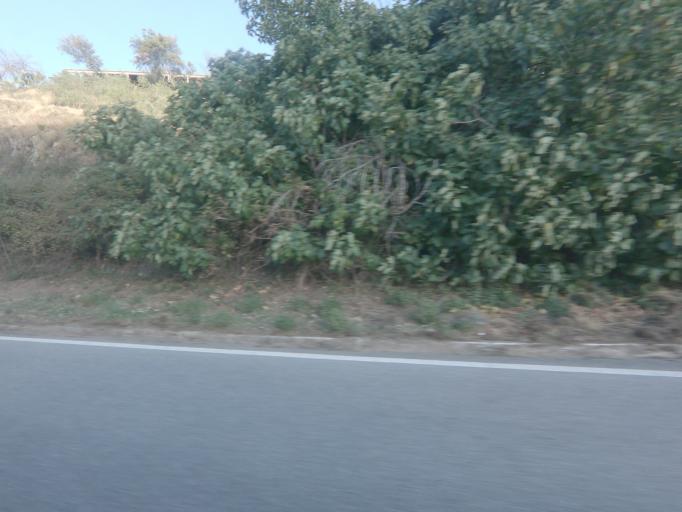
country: PT
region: Viseu
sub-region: Armamar
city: Armamar
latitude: 41.1588
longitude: -7.6693
